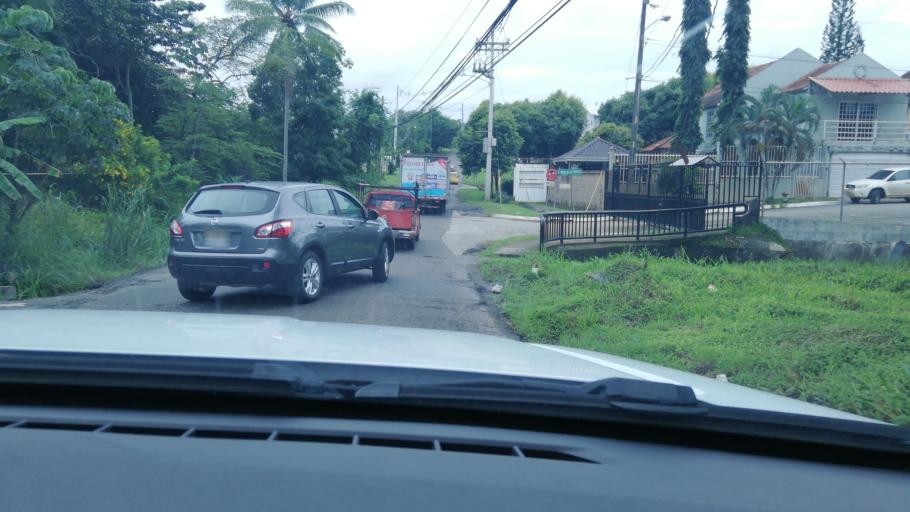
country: PA
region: Panama
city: Las Cumbres
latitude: 9.0754
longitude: -79.5207
